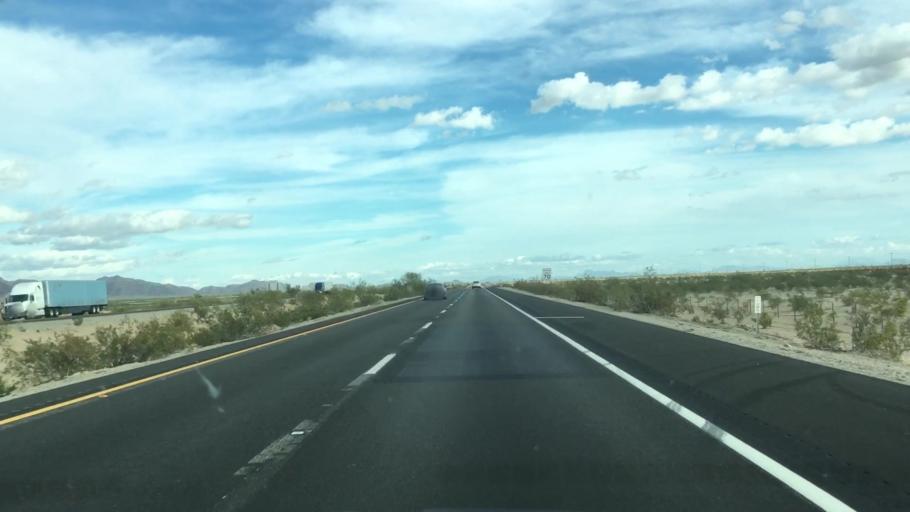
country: US
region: California
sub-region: Riverside County
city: Mesa Verde
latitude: 33.6081
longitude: -114.8854
